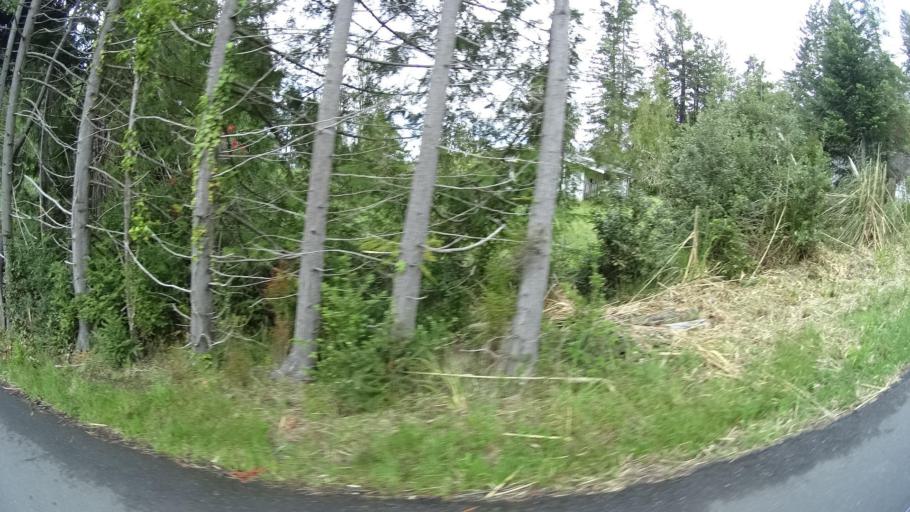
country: US
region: California
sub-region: Humboldt County
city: Bayside
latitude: 40.8251
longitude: -124.0055
